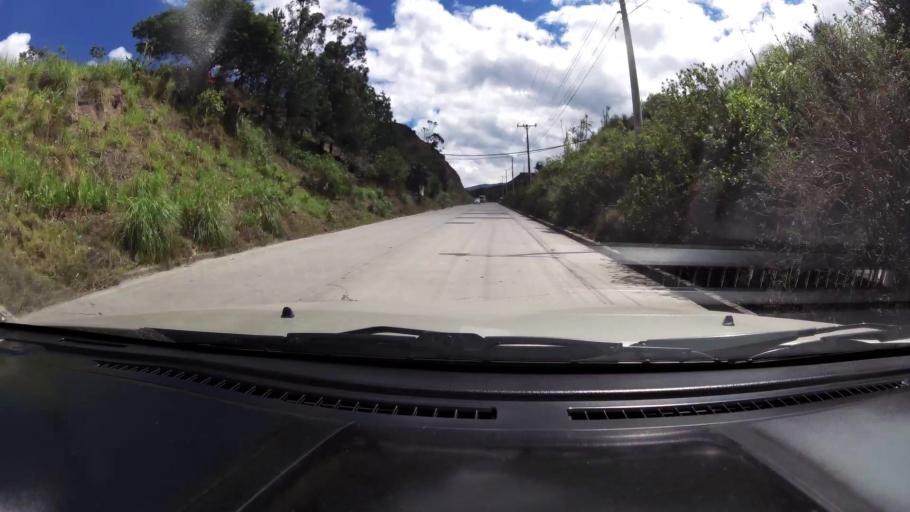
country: EC
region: Azuay
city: Cuenca
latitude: -3.1771
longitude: -79.1659
